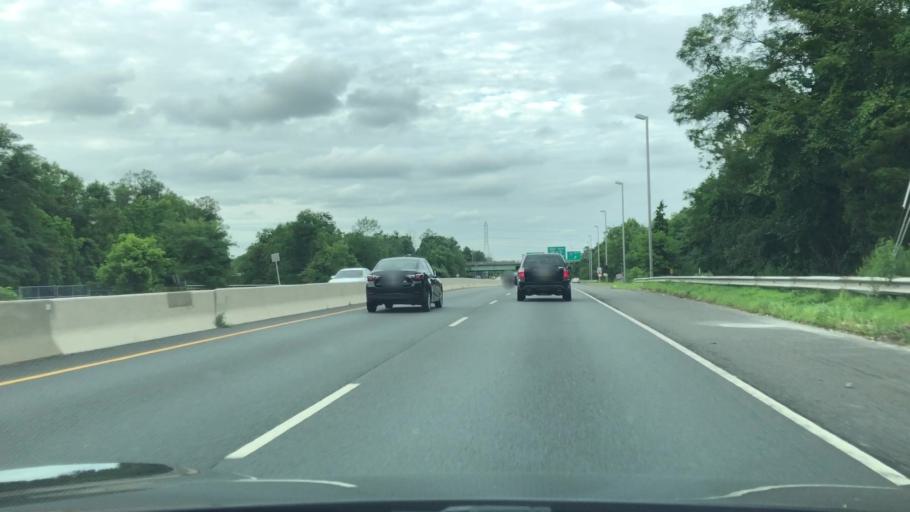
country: US
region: New Jersey
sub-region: Mercer County
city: Lawrenceville
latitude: 40.2800
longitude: -74.7002
